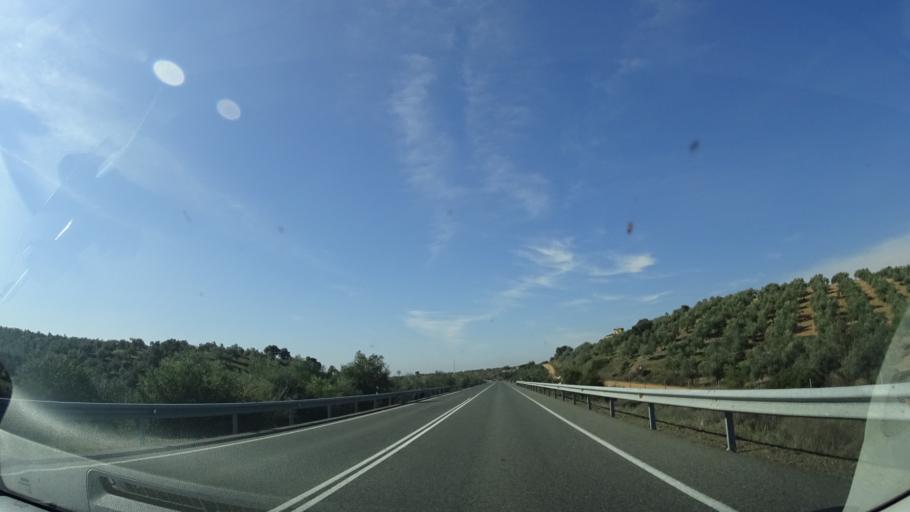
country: ES
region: Andalusia
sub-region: Province of Cordoba
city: Montoro
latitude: 38.0977
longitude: -4.3610
